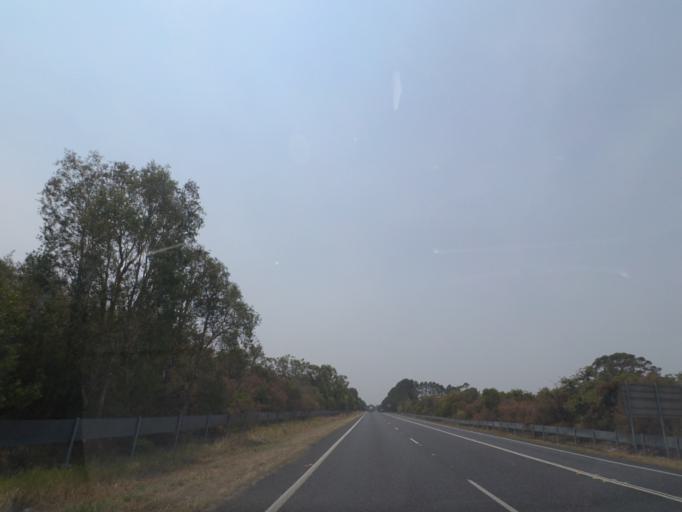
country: AU
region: New South Wales
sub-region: Ballina
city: Ballina
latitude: -28.9436
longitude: 153.4683
